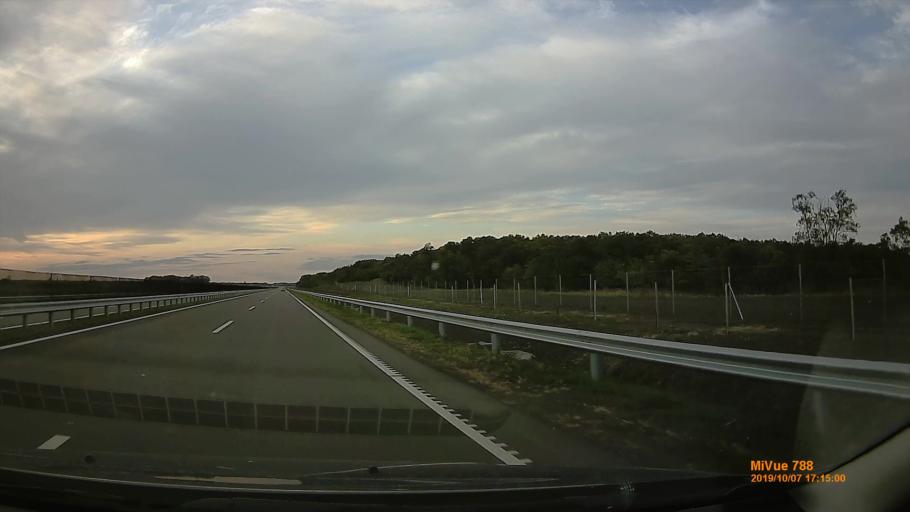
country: HU
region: Jasz-Nagykun-Szolnok
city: Kunszentmarton
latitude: 46.8408
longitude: 20.3374
